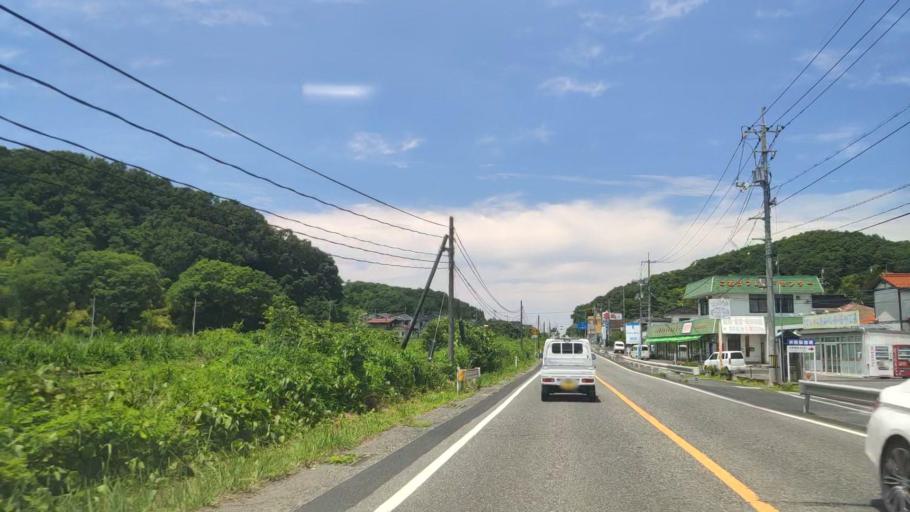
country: JP
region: Tottori
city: Tottori
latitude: 35.4250
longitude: 134.2619
